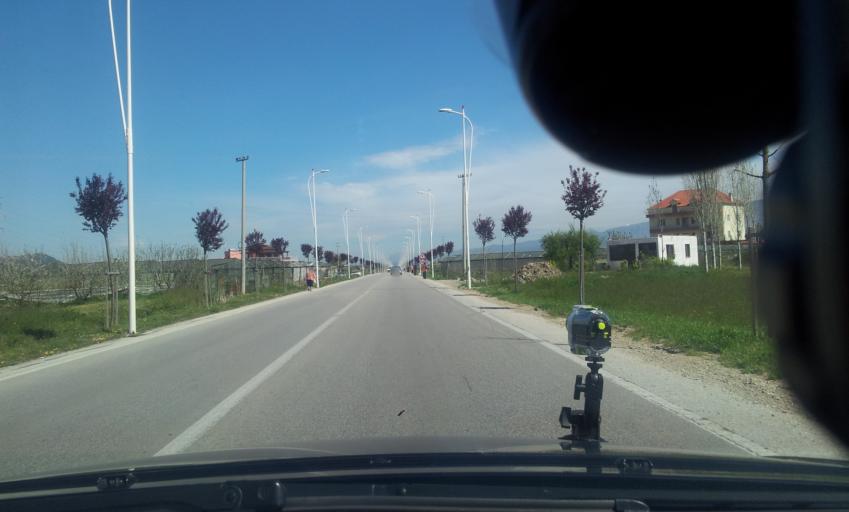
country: AL
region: Tirane
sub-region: Rrethi i Tiranes
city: Berxull
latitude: 41.3769
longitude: 19.7035
